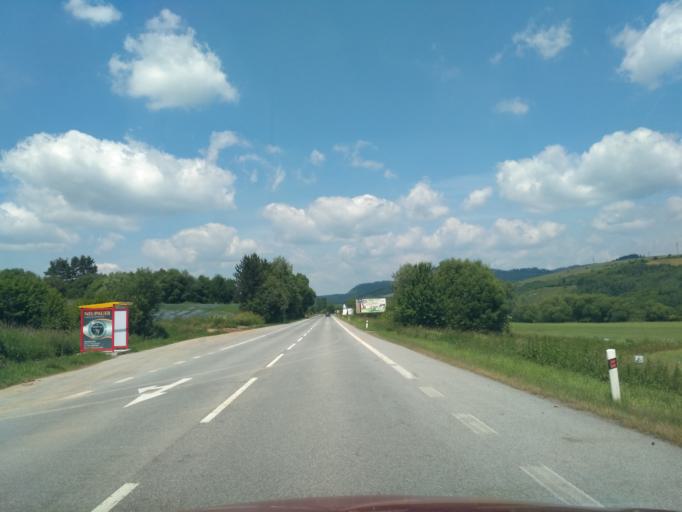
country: SK
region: Presovsky
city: Stara L'ubovna
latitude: 49.2819
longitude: 20.7448
